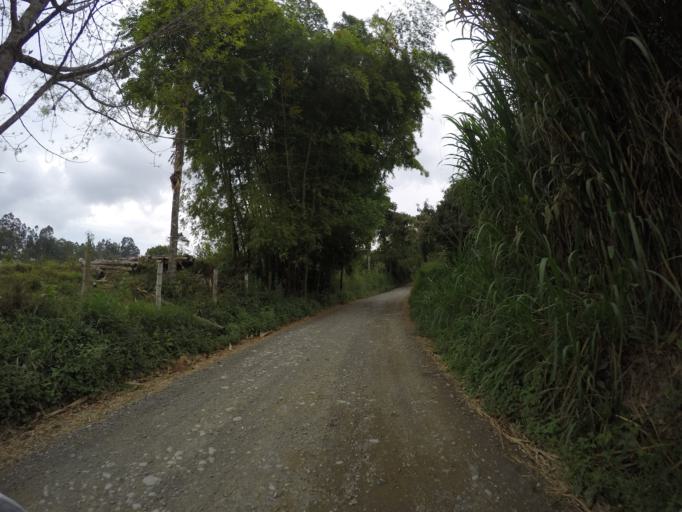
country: CO
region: Quindio
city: Filandia
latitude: 4.6476
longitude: -75.6756
